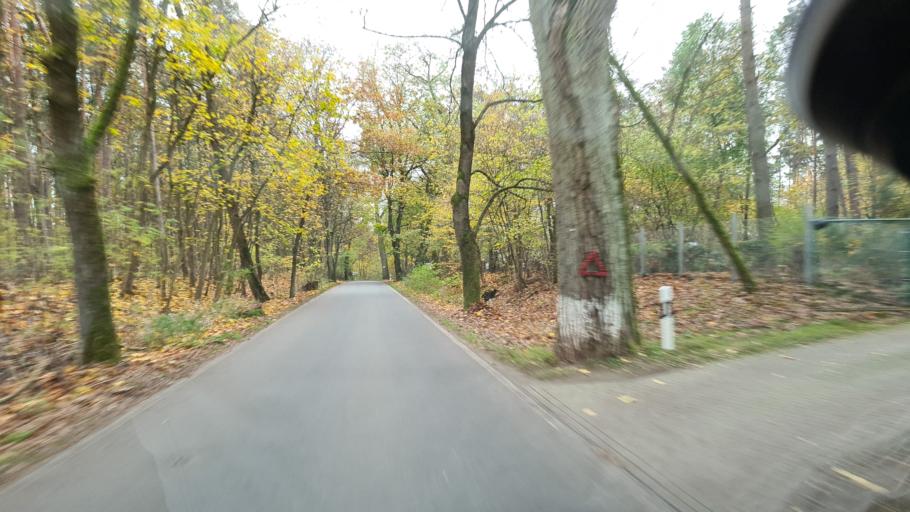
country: DE
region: Brandenburg
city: Lindow
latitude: 52.9568
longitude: 12.9856
